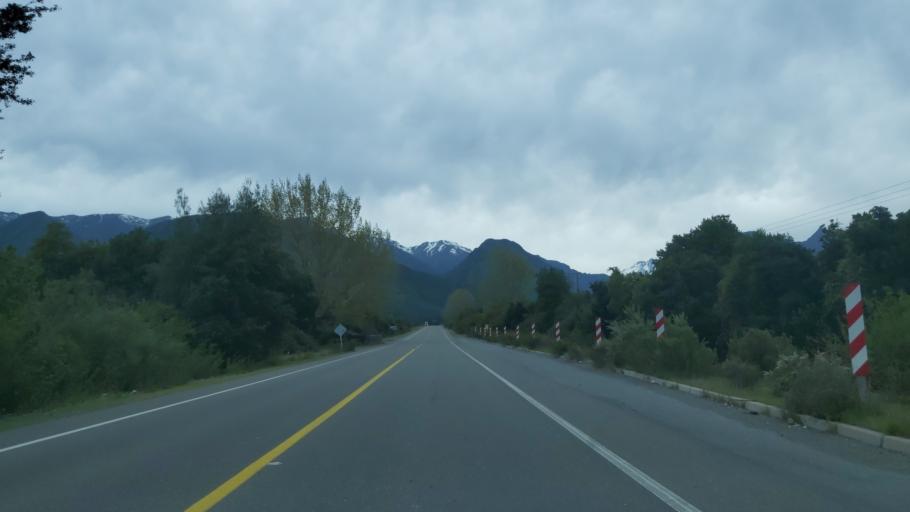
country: CL
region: Maule
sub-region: Provincia de Linares
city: Colbun
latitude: -35.7157
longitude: -71.1163
